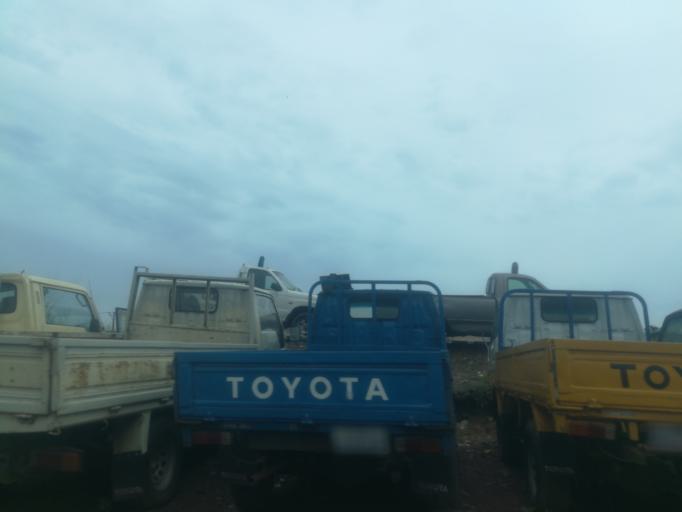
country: NG
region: Oyo
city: Ibadan
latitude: 7.3946
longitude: 3.9379
